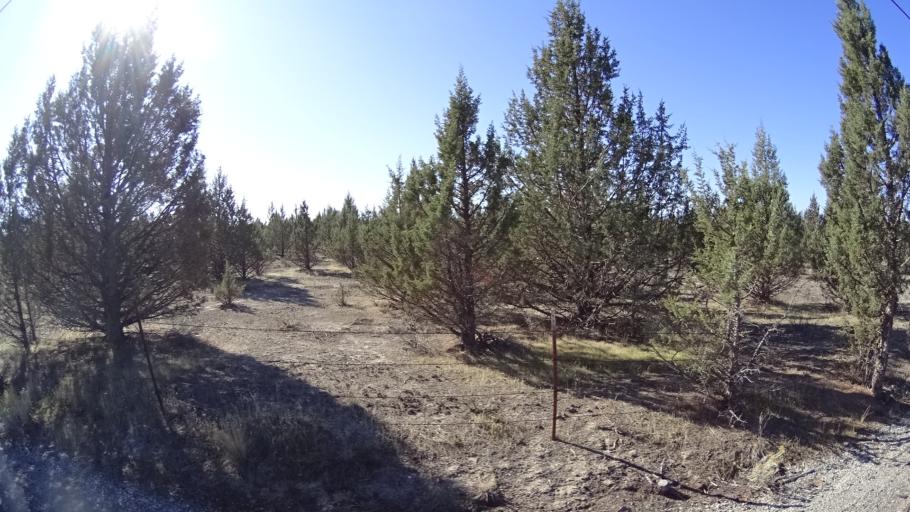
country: US
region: California
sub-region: Siskiyou County
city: Montague
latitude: 41.6439
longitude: -122.3521
